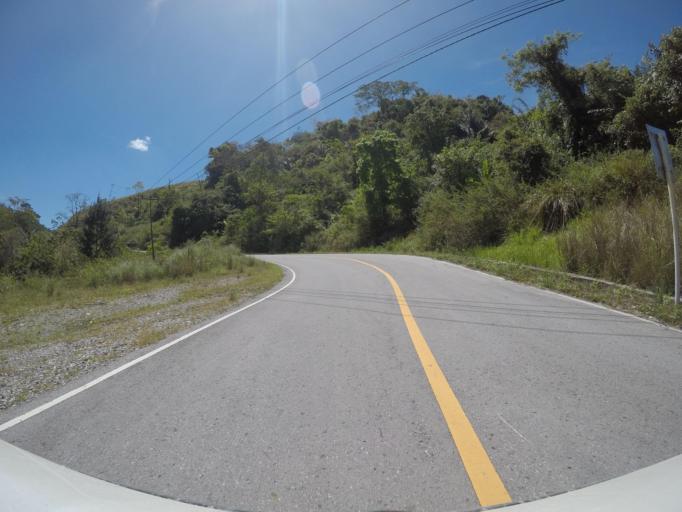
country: TL
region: Manatuto
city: Manatuto
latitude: -8.7658
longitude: 125.9671
